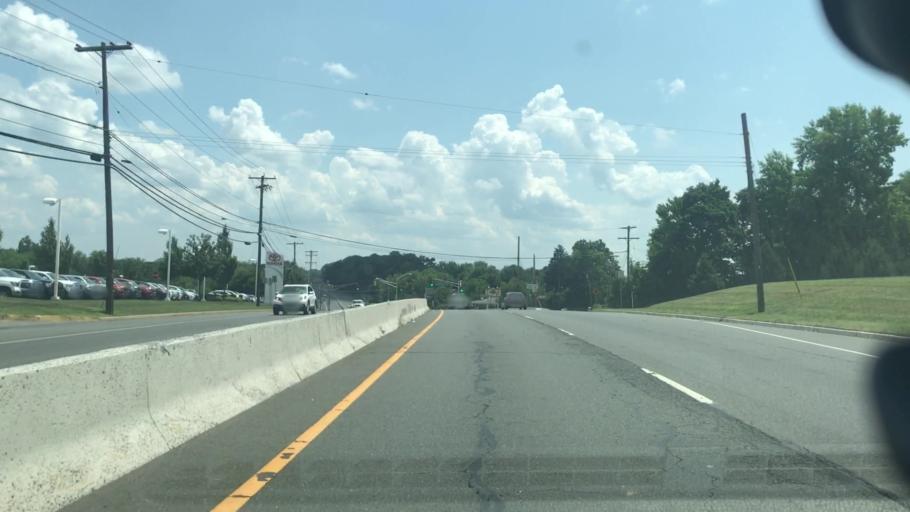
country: US
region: New Jersey
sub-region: Hunterdon County
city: Flemington
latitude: 40.4786
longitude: -74.8639
